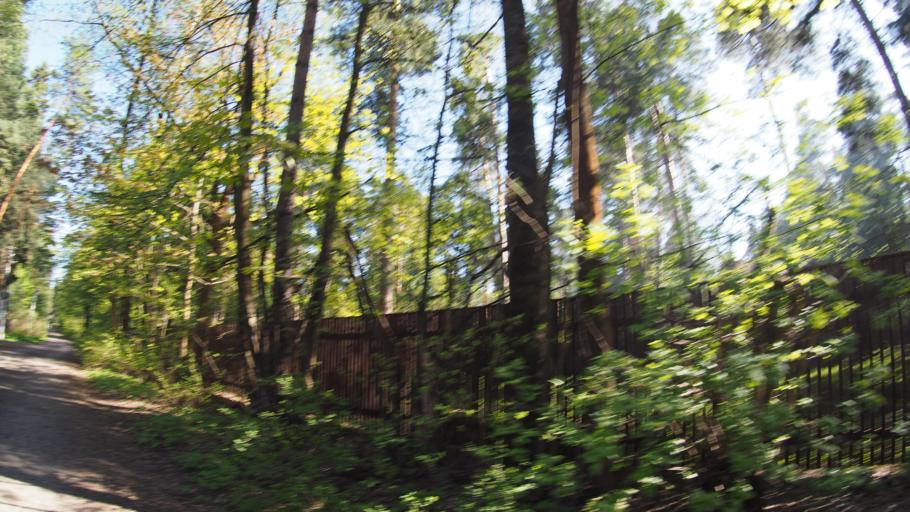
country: RU
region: Moskovskaya
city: Kratovo
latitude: 55.5825
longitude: 38.1753
